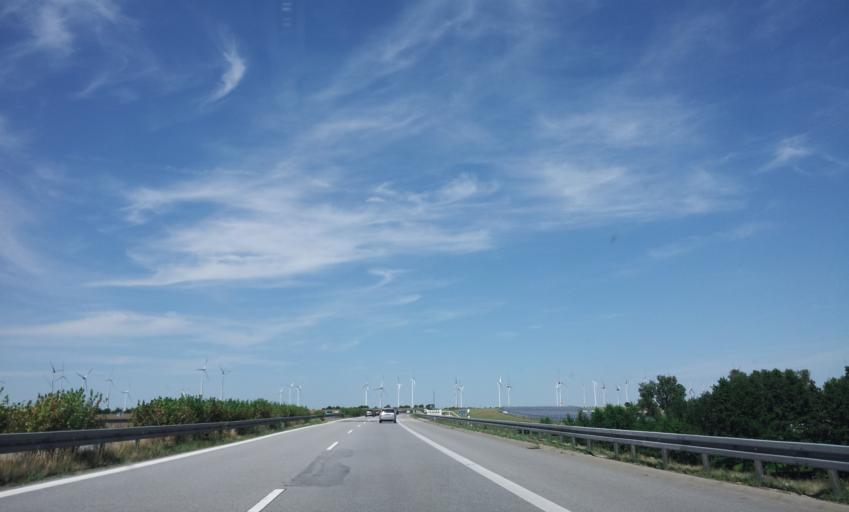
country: DE
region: Mecklenburg-Vorpommern
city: Brunn
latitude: 53.6808
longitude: 13.3316
